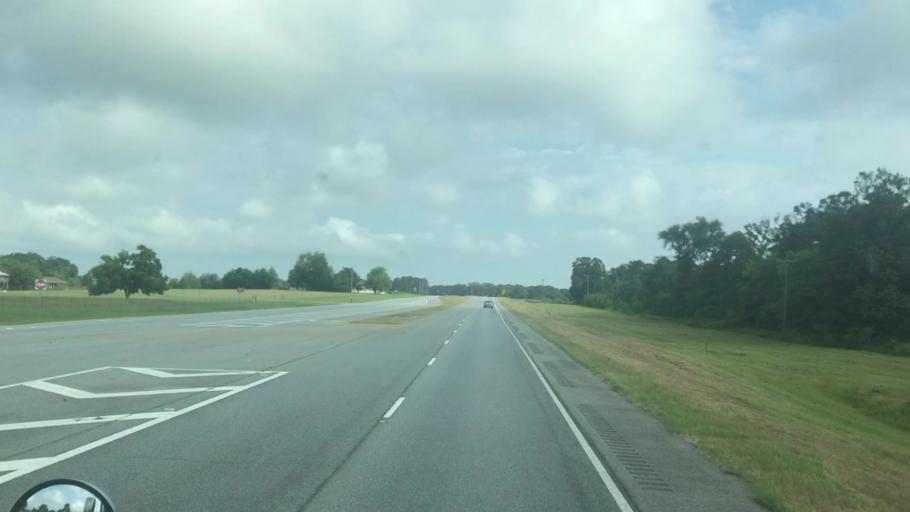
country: US
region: Georgia
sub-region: Miller County
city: Colquitt
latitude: 31.2345
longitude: -84.7848
